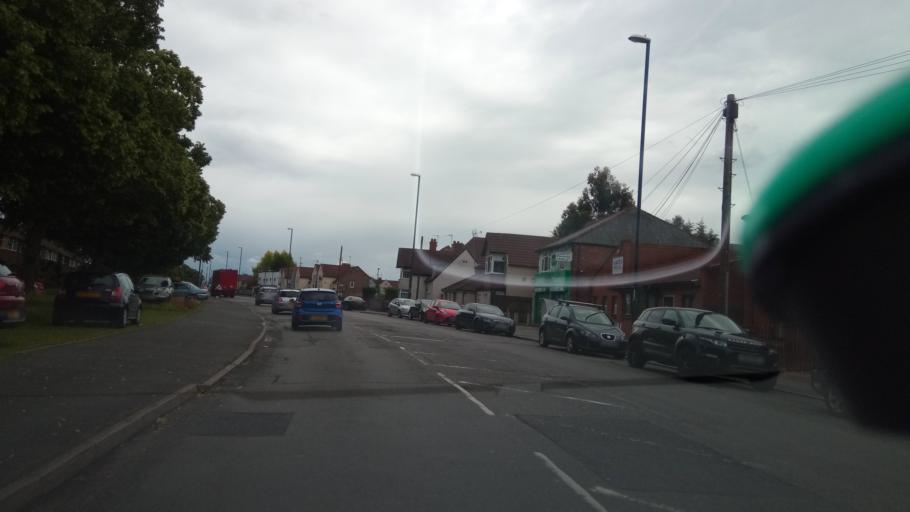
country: GB
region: England
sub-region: Derby
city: Derby
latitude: 52.8963
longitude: -1.4567
